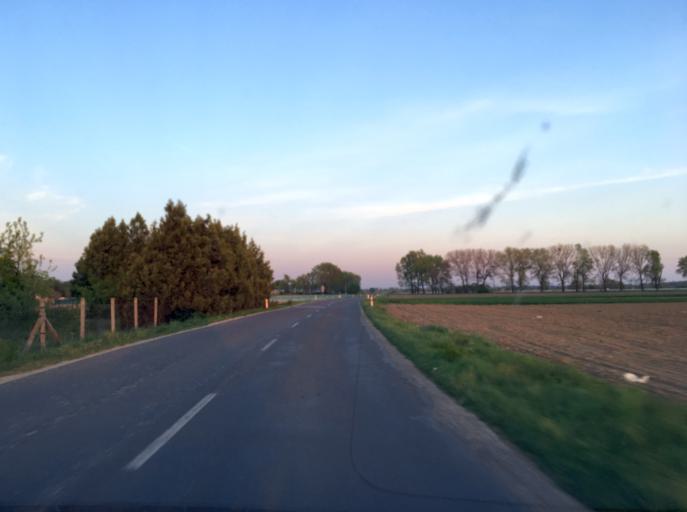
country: SK
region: Nitriansky
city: Kolarovo
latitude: 47.9245
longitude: 18.0277
